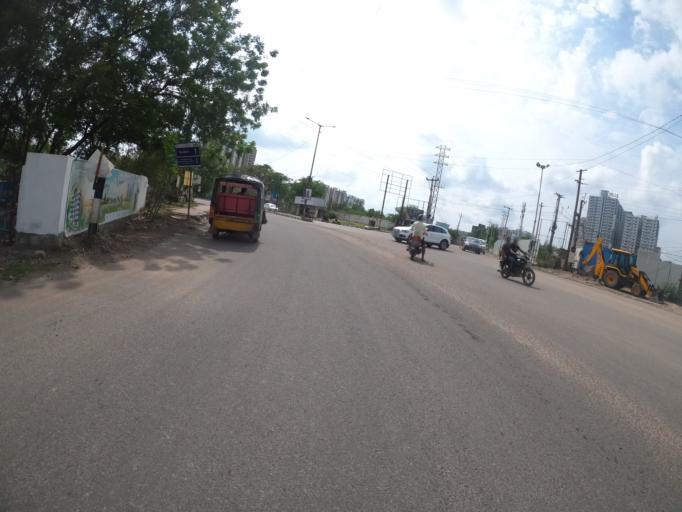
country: IN
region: Telangana
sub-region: Hyderabad
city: Hyderabad
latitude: 17.3880
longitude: 78.3450
